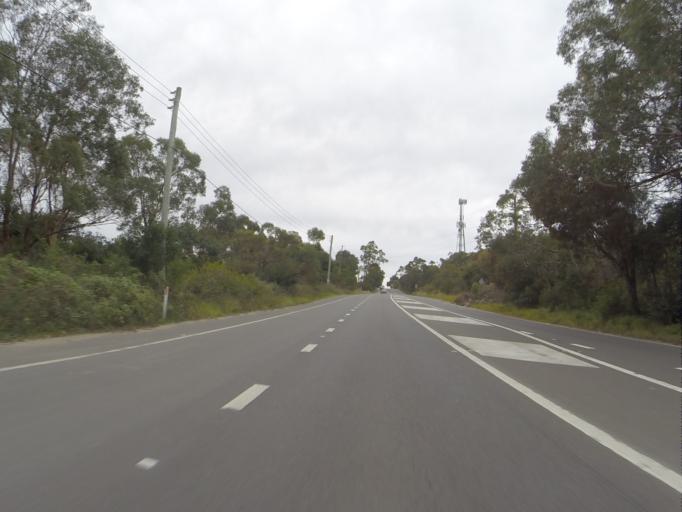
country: AU
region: New South Wales
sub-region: Sutherland Shire
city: Menai
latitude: -34.0367
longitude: 151.0014
